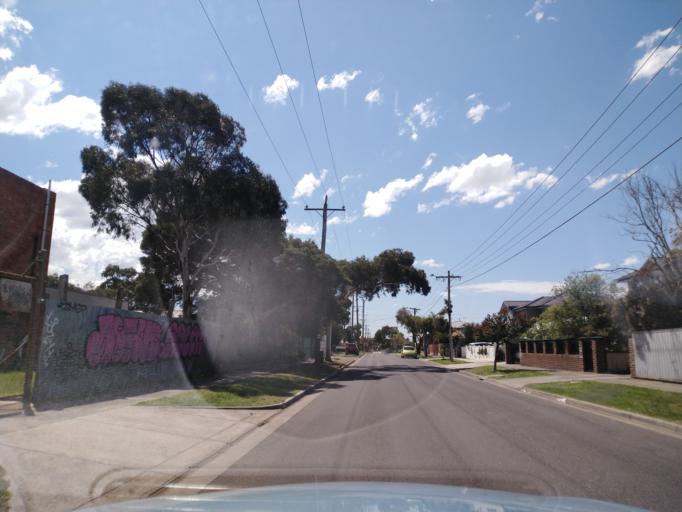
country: AU
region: Victoria
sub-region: Hobsons Bay
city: South Kingsville
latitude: -37.8295
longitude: 144.8668
